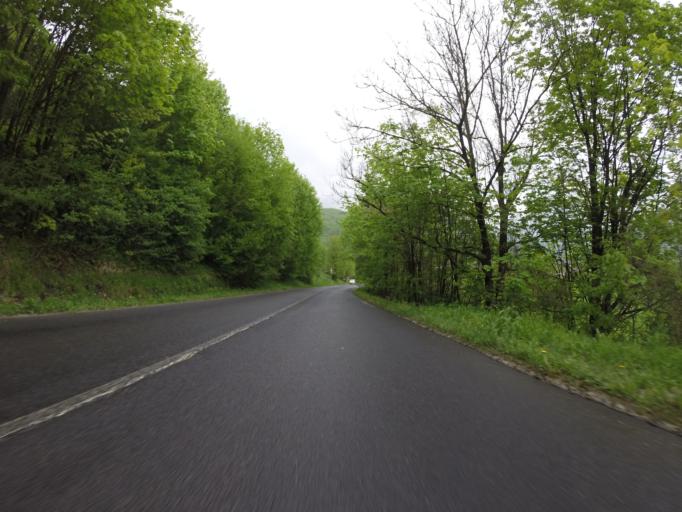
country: SK
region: Banskobystricky
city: Revuca
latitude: 48.7371
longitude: 20.0381
